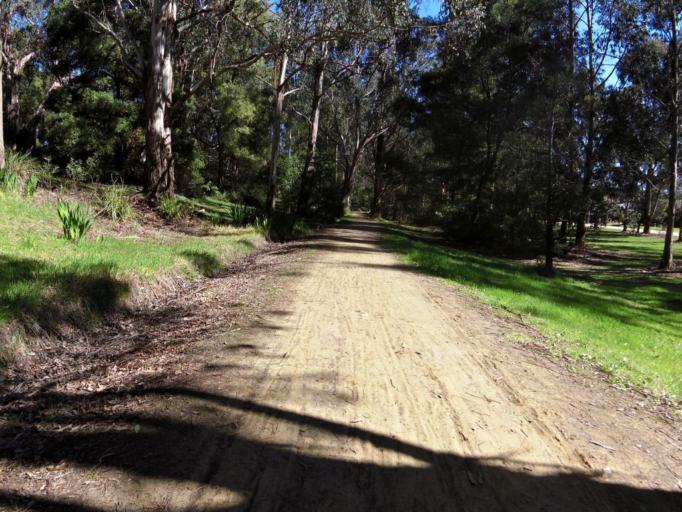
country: AU
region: Victoria
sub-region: Latrobe
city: Morwell
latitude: -38.3795
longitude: 146.2724
